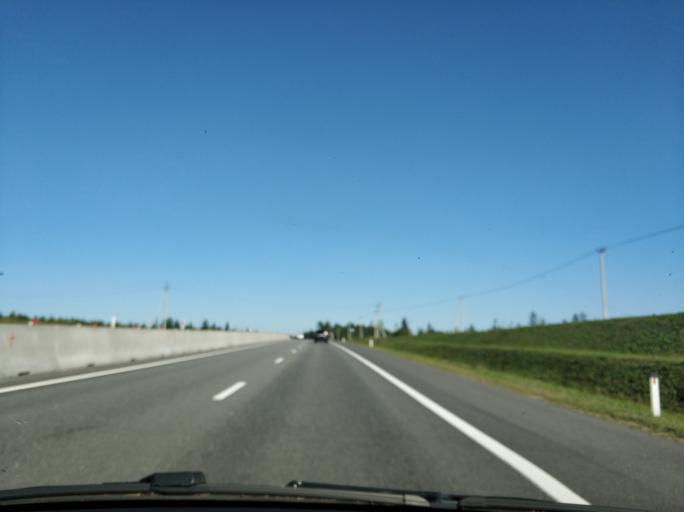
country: RU
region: Leningrad
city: Sosnovo
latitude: 60.5136
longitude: 30.1852
